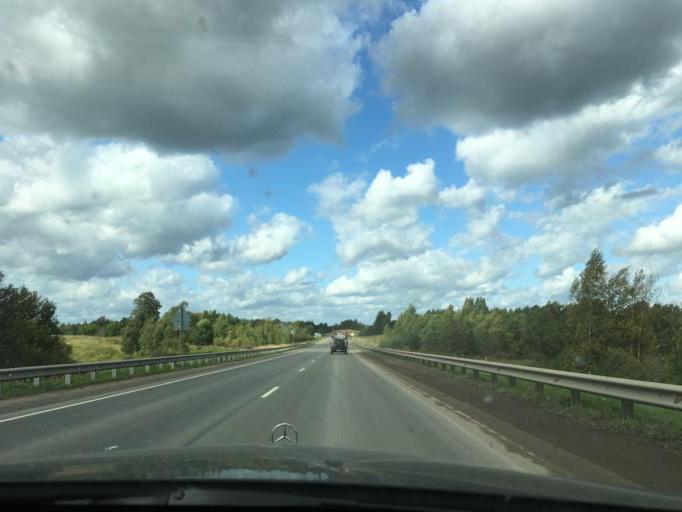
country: RU
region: Pskov
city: Novosokol'niki
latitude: 56.2964
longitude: 30.2272
